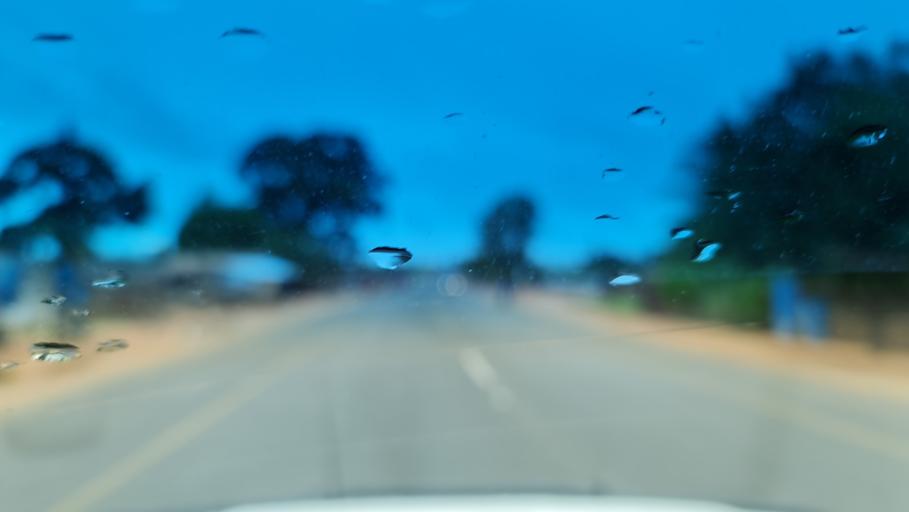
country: MZ
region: Nampula
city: Nampula
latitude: -15.1478
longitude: 39.2990
